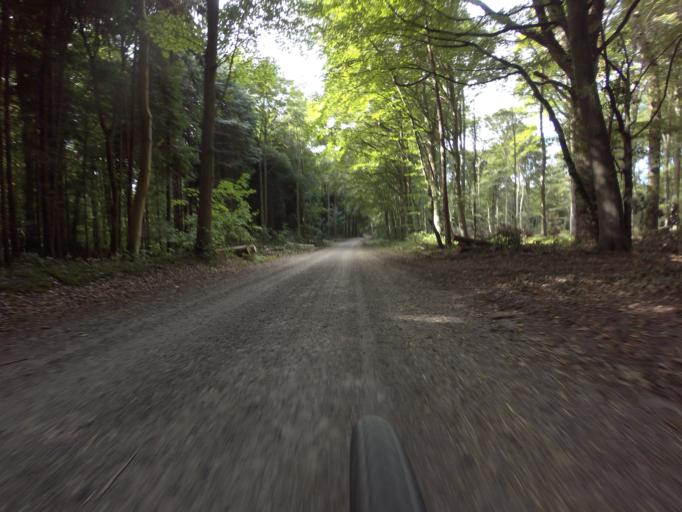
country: DK
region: Zealand
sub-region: Vordingborg Kommune
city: Stege
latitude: 55.0201
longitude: 12.3914
